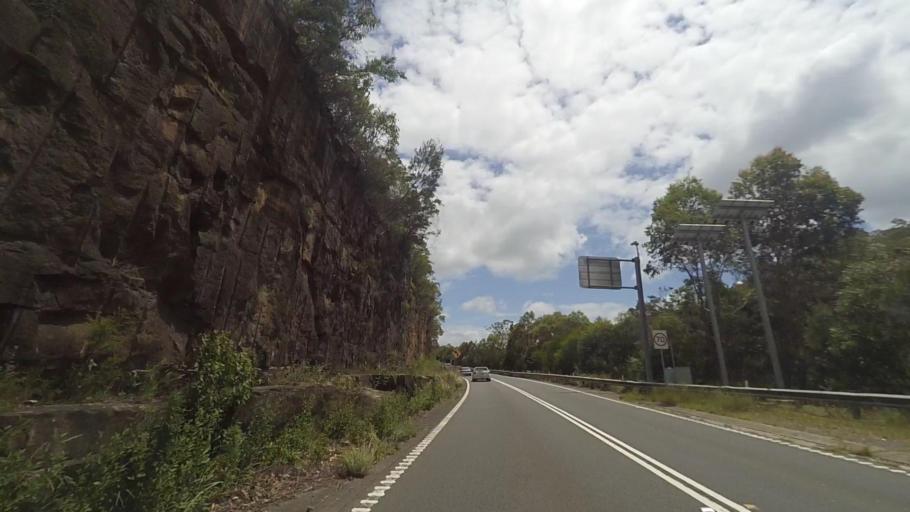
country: AU
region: New South Wales
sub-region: Sutherland Shire
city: Engadine
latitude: -34.0609
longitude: 150.9960
